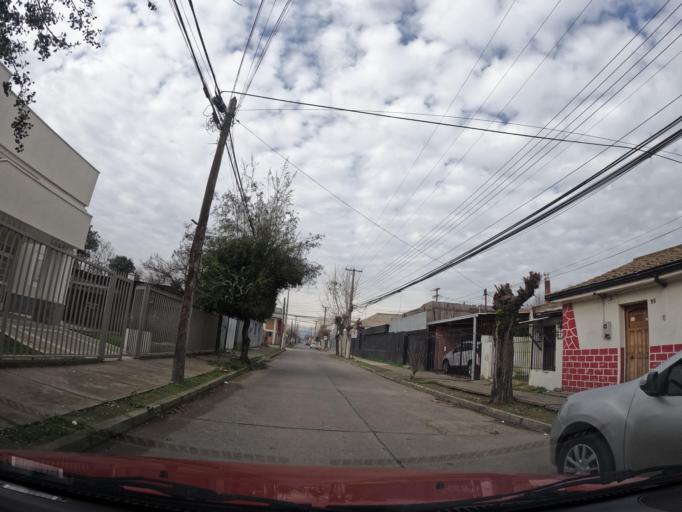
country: CL
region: Maule
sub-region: Provincia de Linares
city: Linares
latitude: -35.8428
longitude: -71.6016
